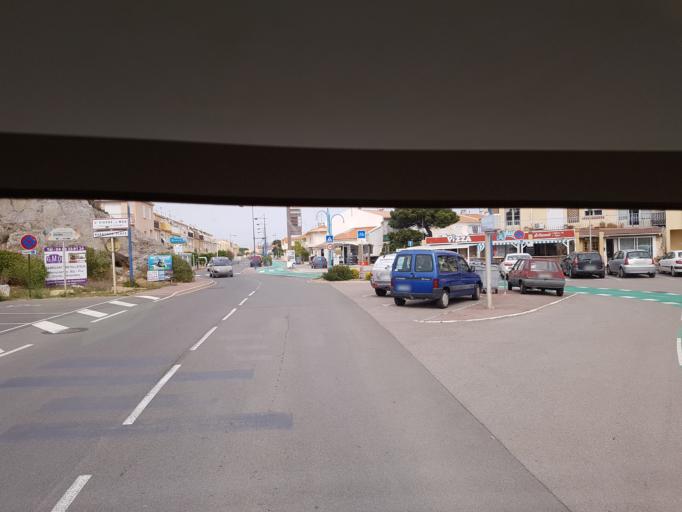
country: FR
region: Languedoc-Roussillon
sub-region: Departement de l'Aude
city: Fleury
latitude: 43.1712
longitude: 3.1809
